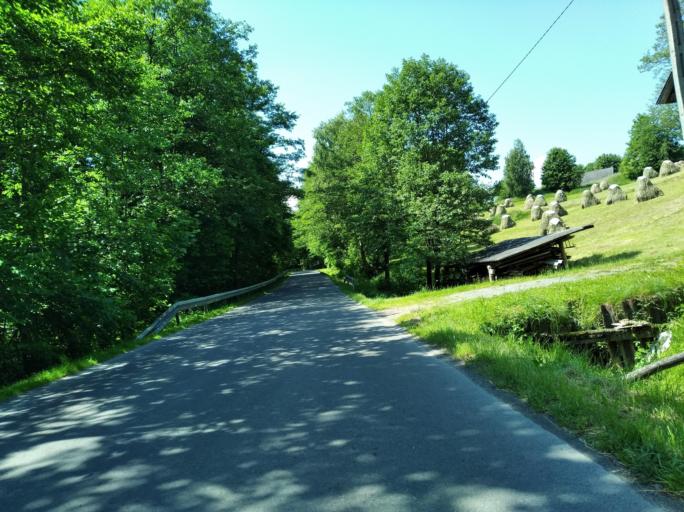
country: PL
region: Subcarpathian Voivodeship
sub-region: Powiat ropczycko-sedziszowski
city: Zagorzyce
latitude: 49.9823
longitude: 21.6471
